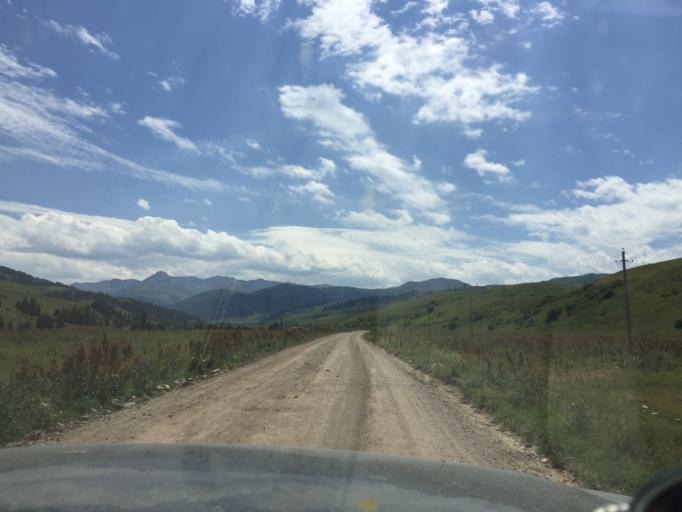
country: KZ
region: Almaty Oblysy
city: Kegen
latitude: 42.7308
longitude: 79.1693
